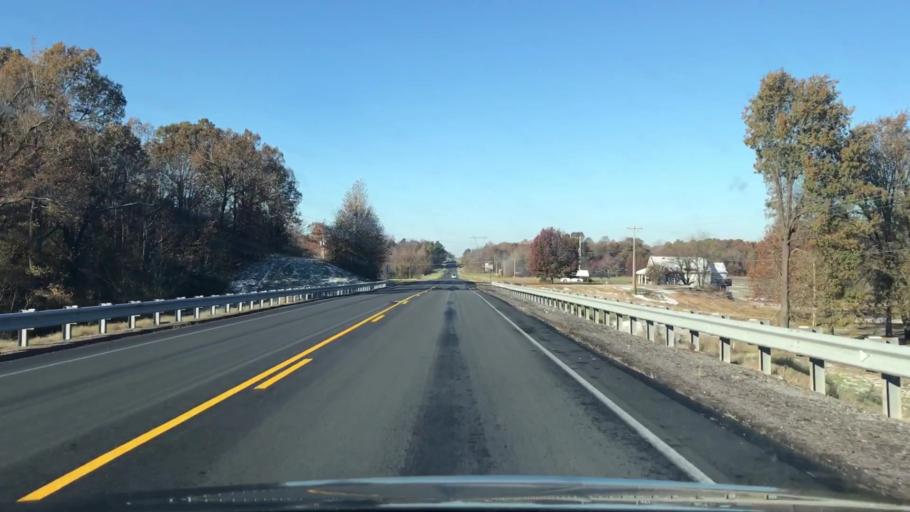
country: US
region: Kentucky
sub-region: Marshall County
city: Calvert City
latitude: 37.0053
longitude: -88.4028
